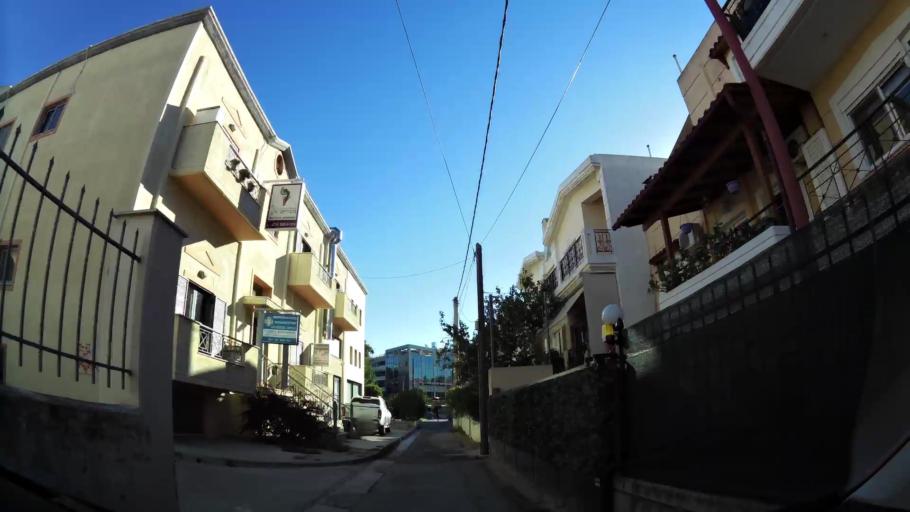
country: GR
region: Attica
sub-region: Nomarchia Anatolikis Attikis
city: Gerakas
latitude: 38.0097
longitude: 23.8563
